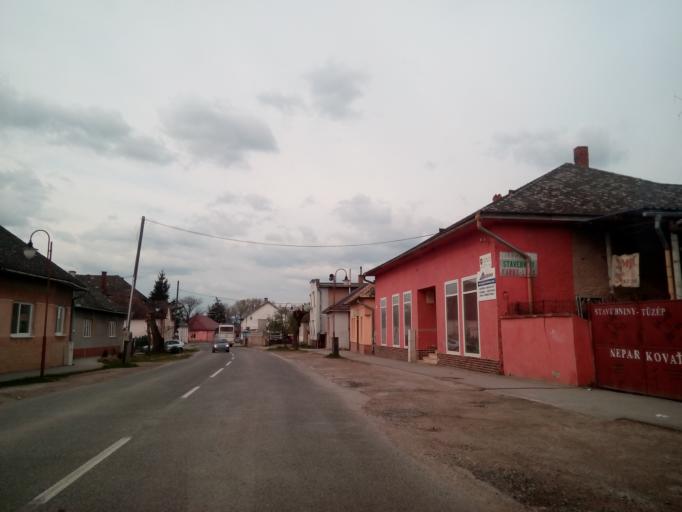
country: SK
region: Kosicky
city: Medzev
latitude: 48.5998
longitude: 20.8766
